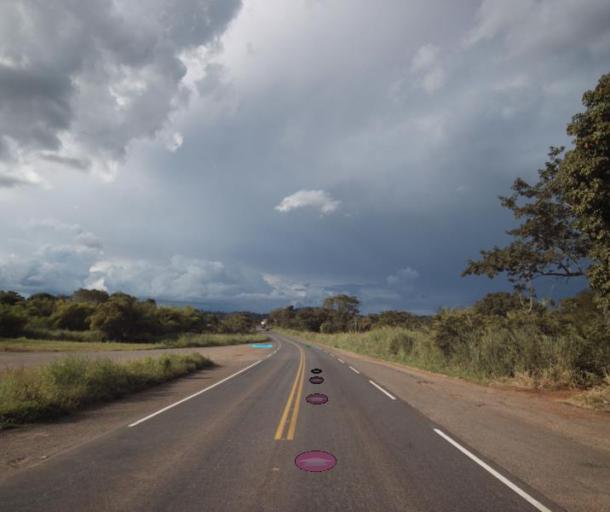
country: BR
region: Goias
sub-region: Rialma
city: Rialma
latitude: -15.2754
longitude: -49.5515
